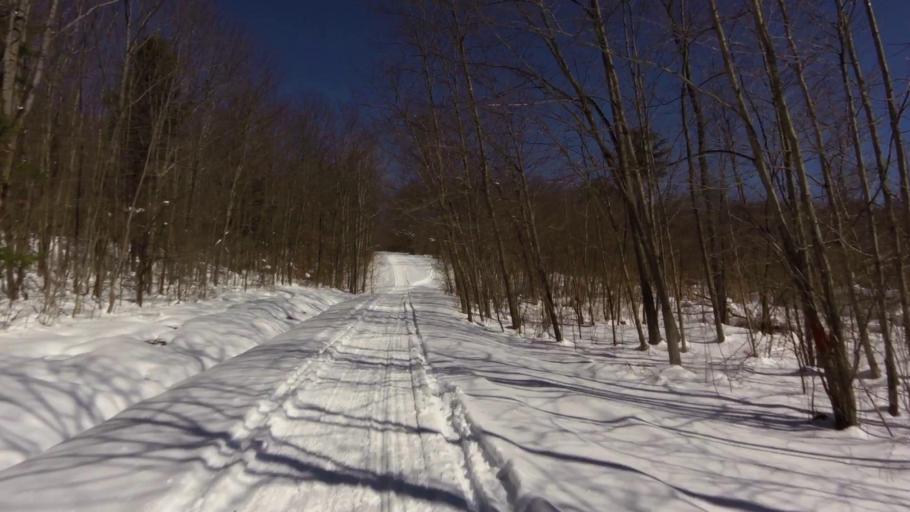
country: US
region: New York
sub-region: Allegany County
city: Cuba
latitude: 42.3164
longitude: -78.2310
